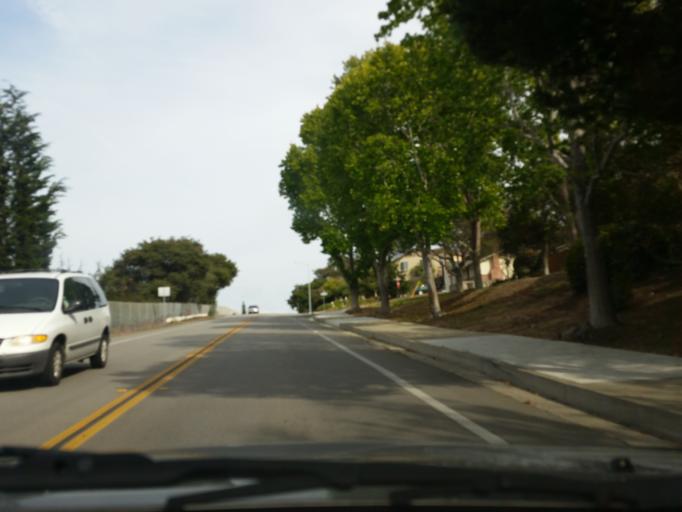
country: US
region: California
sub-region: San Luis Obispo County
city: Arroyo Grande
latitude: 35.1279
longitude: -120.6013
